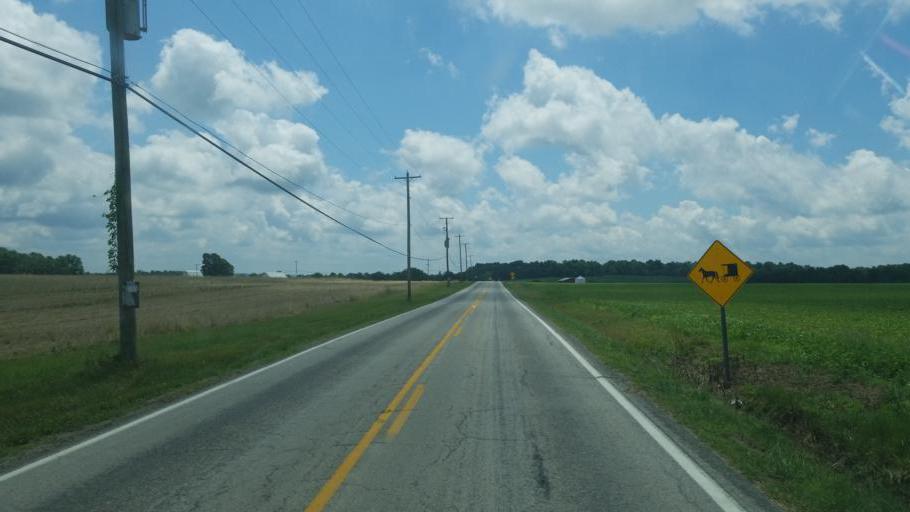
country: US
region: Ohio
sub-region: Highland County
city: Greenfield
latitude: 39.2478
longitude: -83.4397
